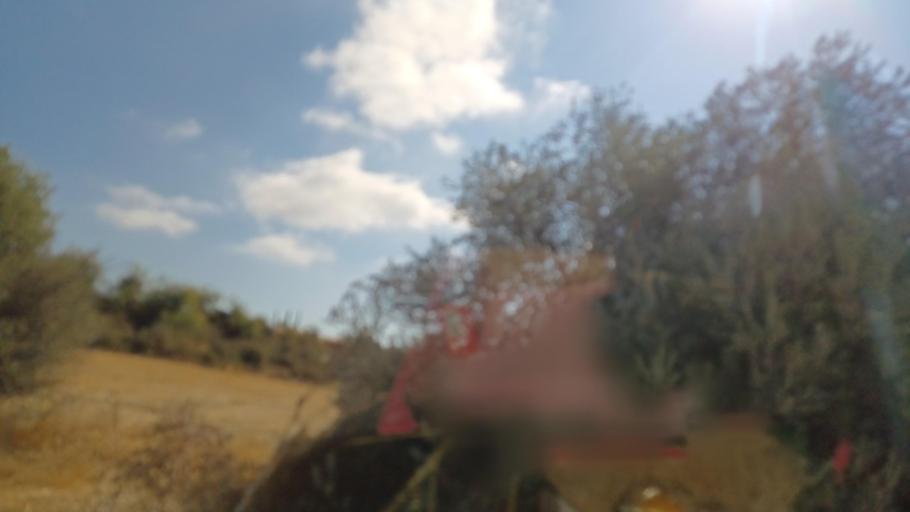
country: CY
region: Pafos
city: Polis
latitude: 35.0427
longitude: 32.4449
